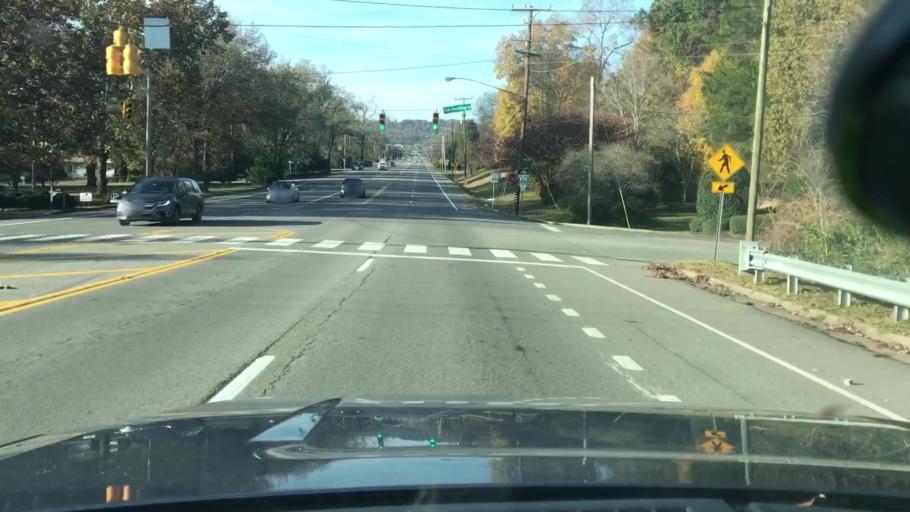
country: US
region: Tennessee
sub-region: Davidson County
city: Belle Meade
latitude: 36.0974
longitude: -86.8756
